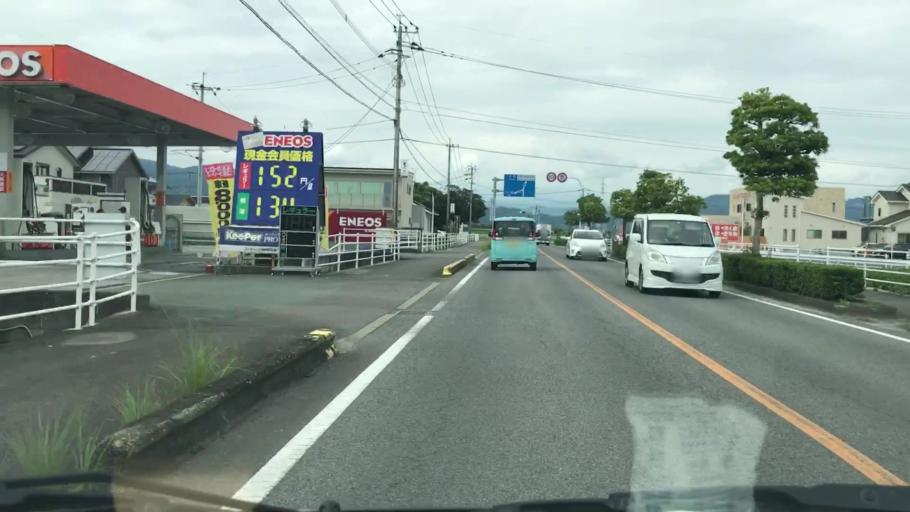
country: JP
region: Saga Prefecture
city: Saga-shi
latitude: 33.2743
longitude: 130.2608
